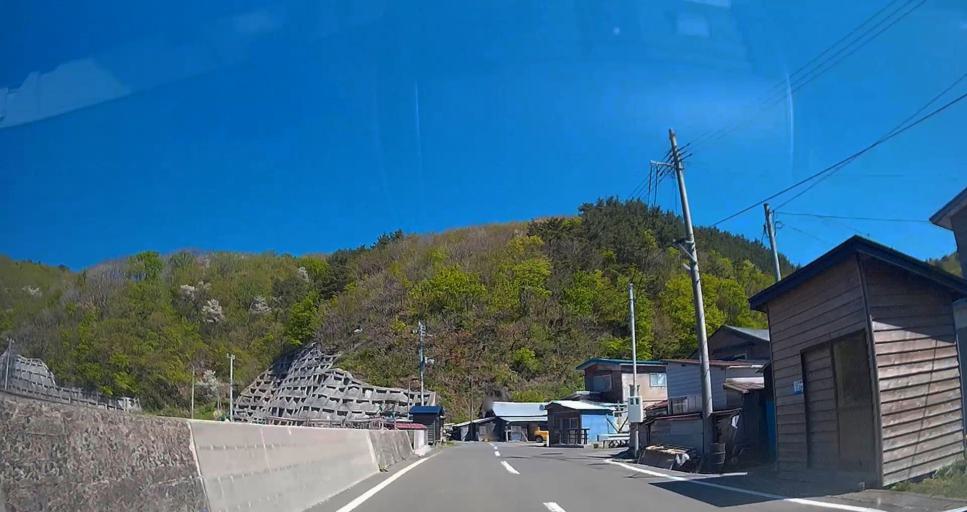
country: JP
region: Aomori
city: Aomori Shi
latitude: 41.1382
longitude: 140.7792
